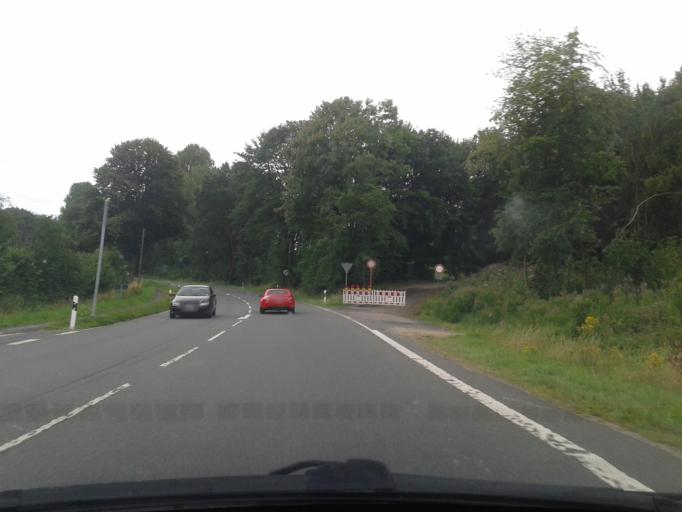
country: DE
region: North Rhine-Westphalia
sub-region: Regierungsbezirk Detmold
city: Horn
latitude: 51.8969
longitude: 8.9367
